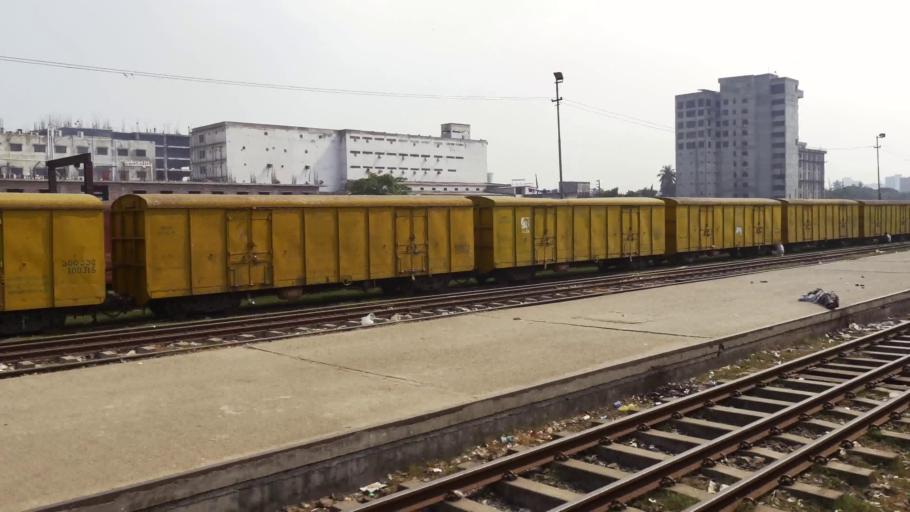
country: BD
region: Dhaka
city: Paltan
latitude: 23.7934
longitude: 90.4003
